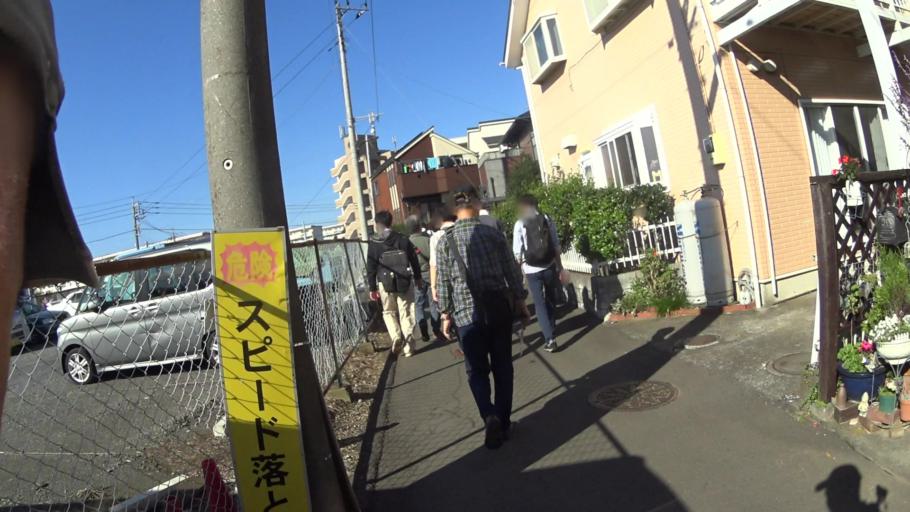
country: JP
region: Tokyo
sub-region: Machida-shi
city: Machida
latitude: 35.5702
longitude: 139.4388
